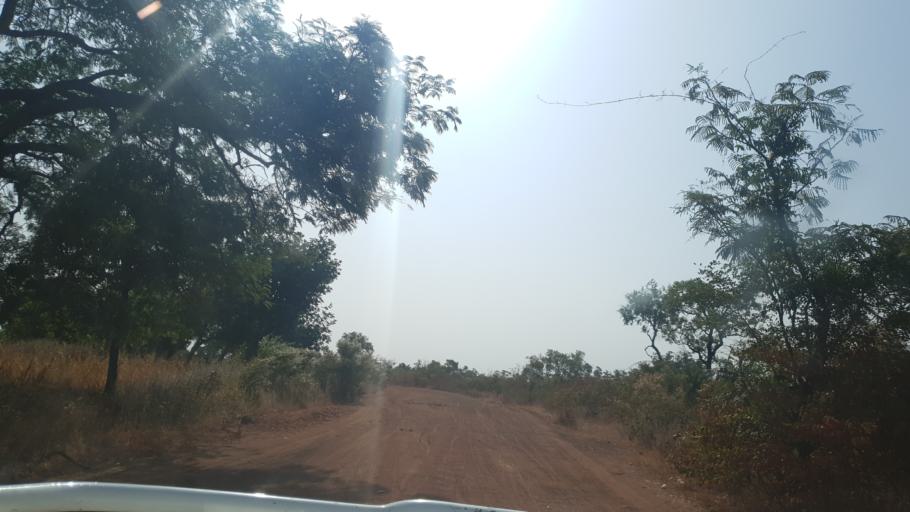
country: ML
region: Koulikoro
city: Dioila
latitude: 12.6686
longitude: -6.7015
